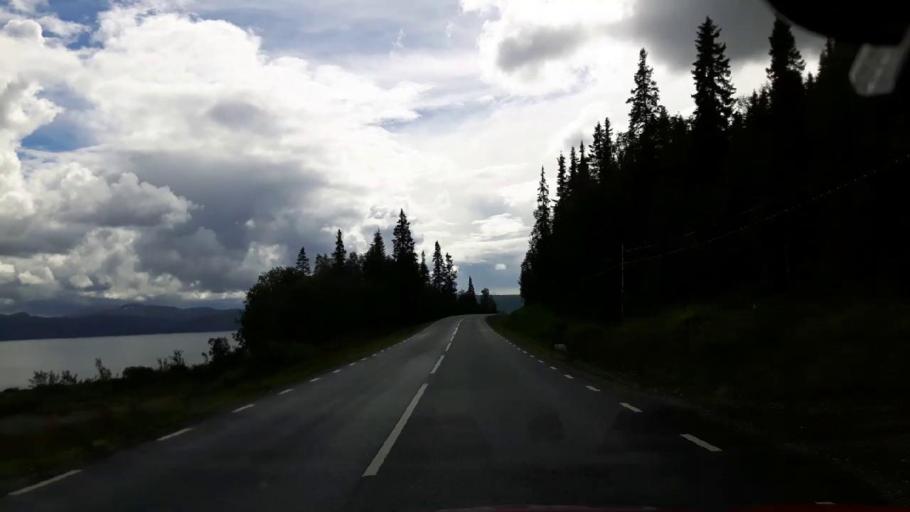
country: NO
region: Nord-Trondelag
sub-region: Royrvik
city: Royrvik
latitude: 64.8324
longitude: 14.0777
